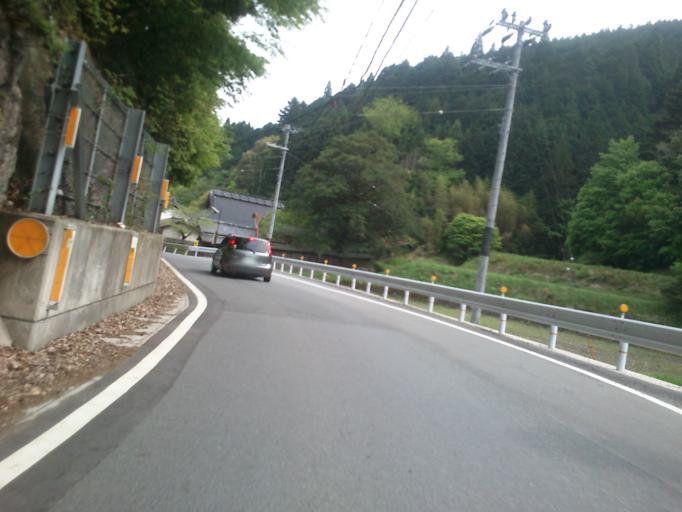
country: JP
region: Kyoto
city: Kameoka
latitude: 34.9465
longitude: 135.5491
